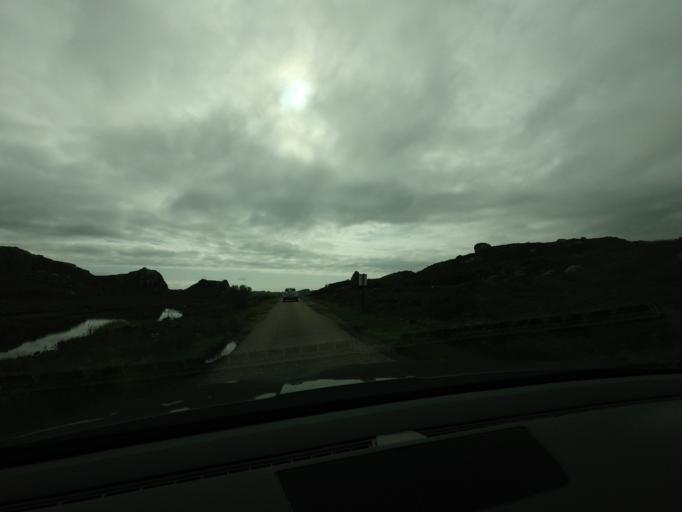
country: GB
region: Scotland
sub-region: Highland
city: Ullapool
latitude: 58.4295
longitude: -4.9738
